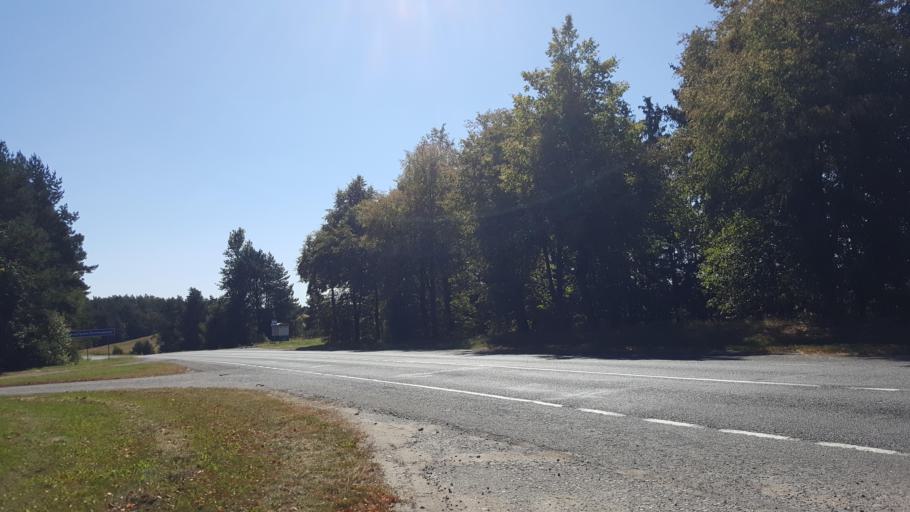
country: PL
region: Lublin Voivodeship
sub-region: Powiat bialski
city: Terespol
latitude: 52.2321
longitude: 23.5084
